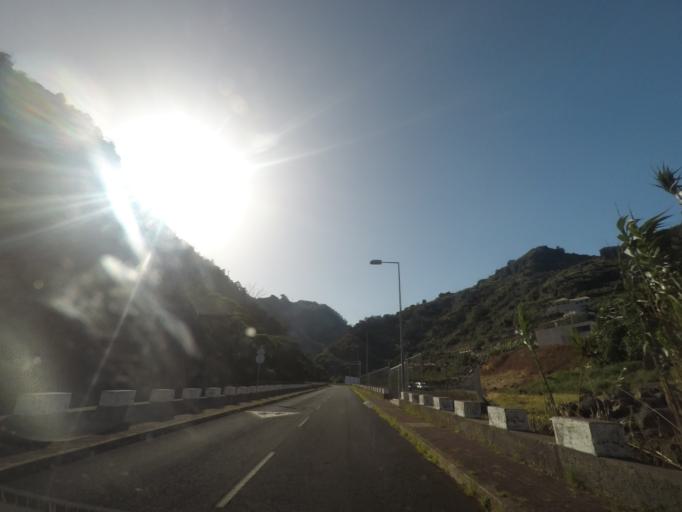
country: PT
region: Madeira
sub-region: Santa Cruz
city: Santa Cruz
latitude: 32.6911
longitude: -16.7990
